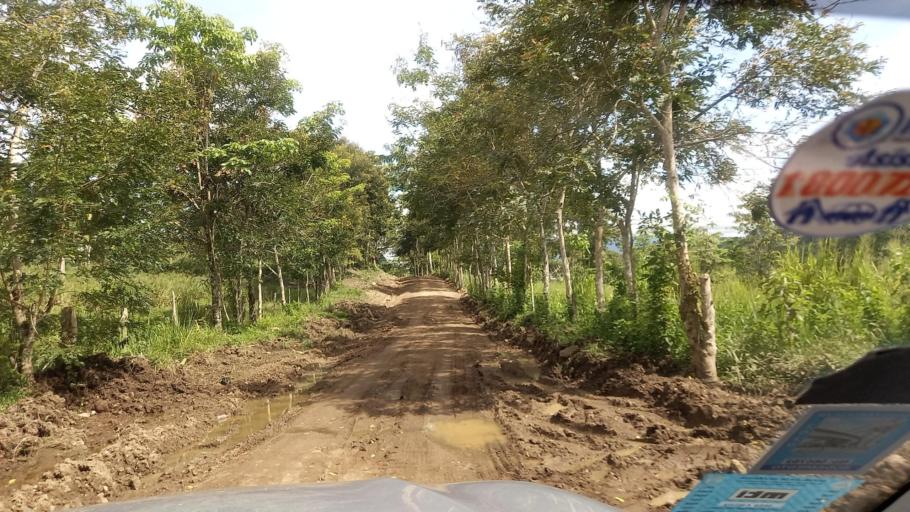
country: NI
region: Jinotega
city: San Jose de Bocay
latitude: 13.3840
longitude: -85.6885
